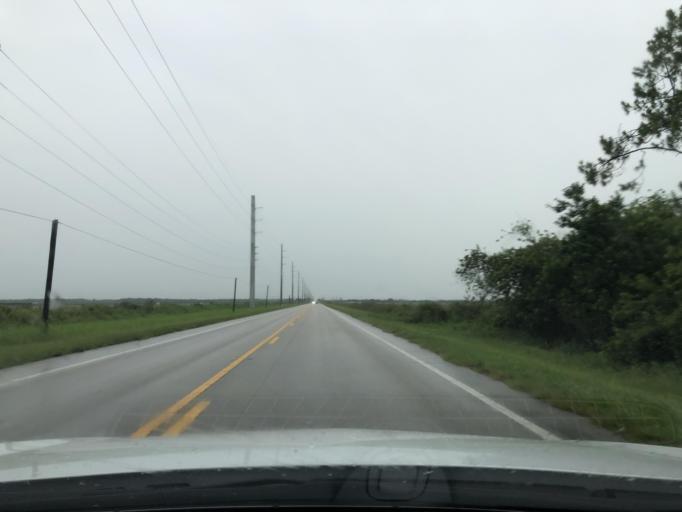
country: US
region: Florida
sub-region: Collier County
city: Orangetree
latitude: 26.2938
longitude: -81.4950
